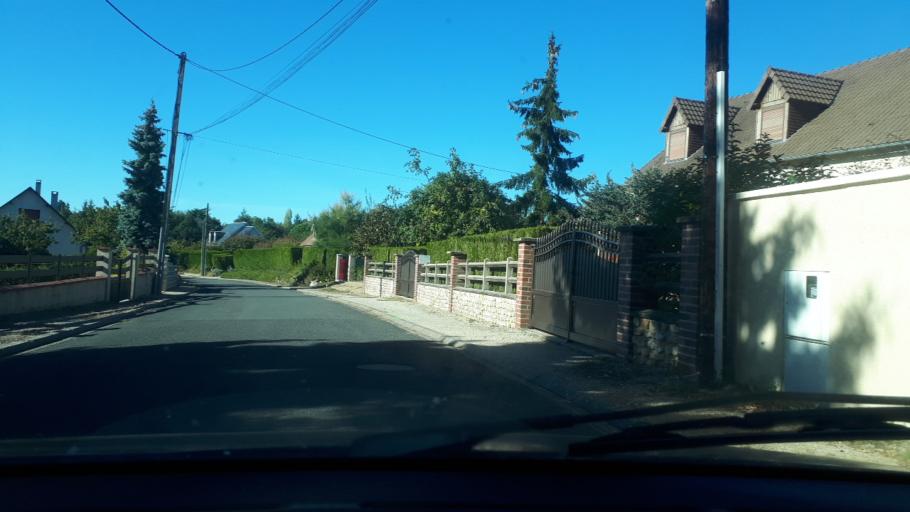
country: FR
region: Centre
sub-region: Departement du Loir-et-Cher
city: Villiers-sur-Loir
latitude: 47.8066
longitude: 0.9993
